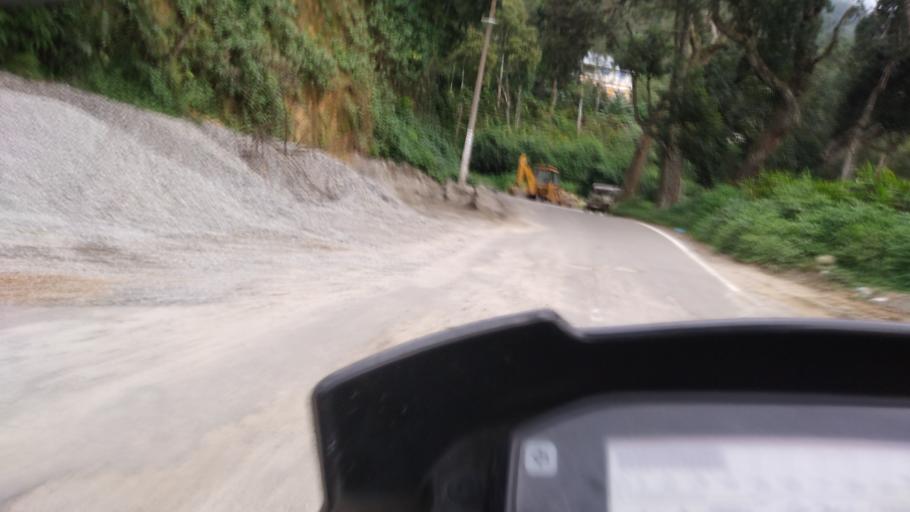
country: IN
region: Tamil Nadu
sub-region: Theni
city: Bodinayakkanur
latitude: 10.0070
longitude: 77.2303
